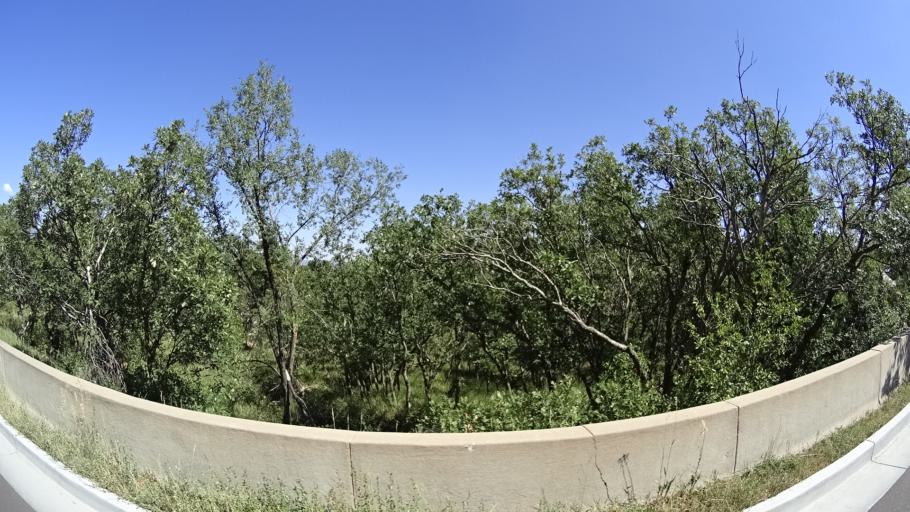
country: US
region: Colorado
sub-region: El Paso County
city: Colorado Springs
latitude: 38.7747
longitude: -104.8542
